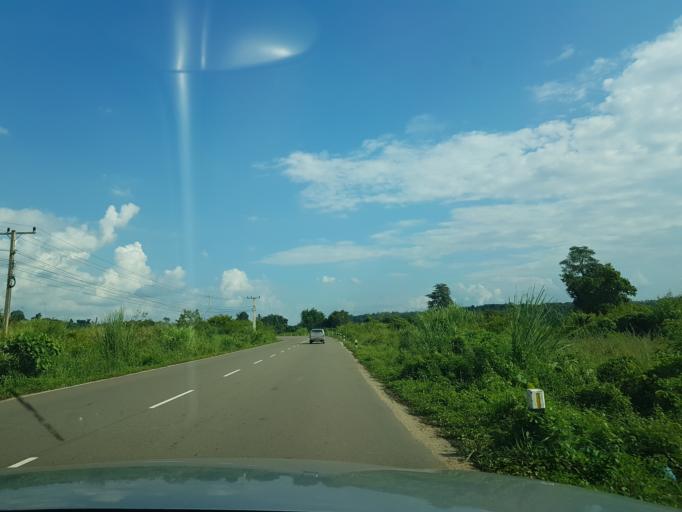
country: TH
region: Nong Khai
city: Pho Tak
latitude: 17.9957
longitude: 102.4169
